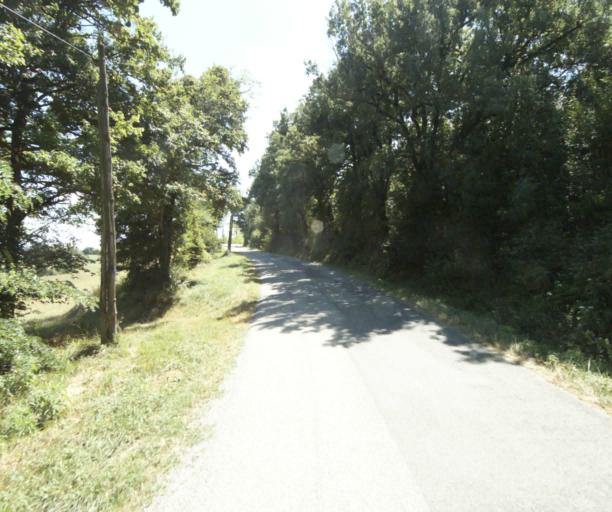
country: FR
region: Midi-Pyrenees
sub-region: Departement de la Haute-Garonne
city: Saint-Felix-Lauragais
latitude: 43.4811
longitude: 1.8697
